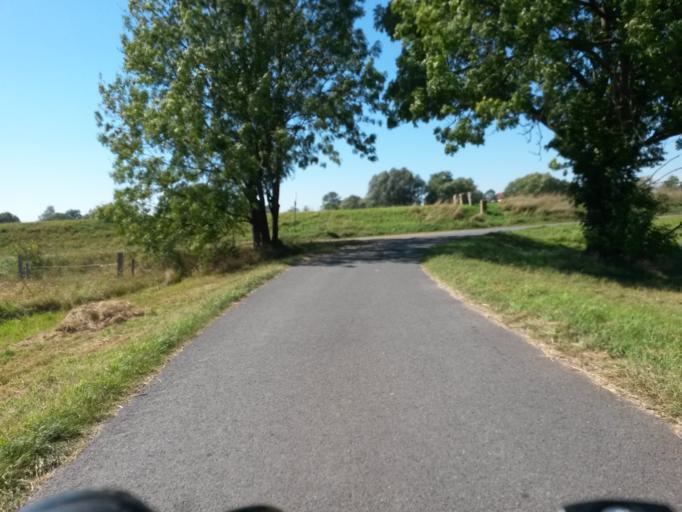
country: PL
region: West Pomeranian Voivodeship
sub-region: Powiat gryfinski
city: Cedynia
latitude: 52.9223
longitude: 14.1293
